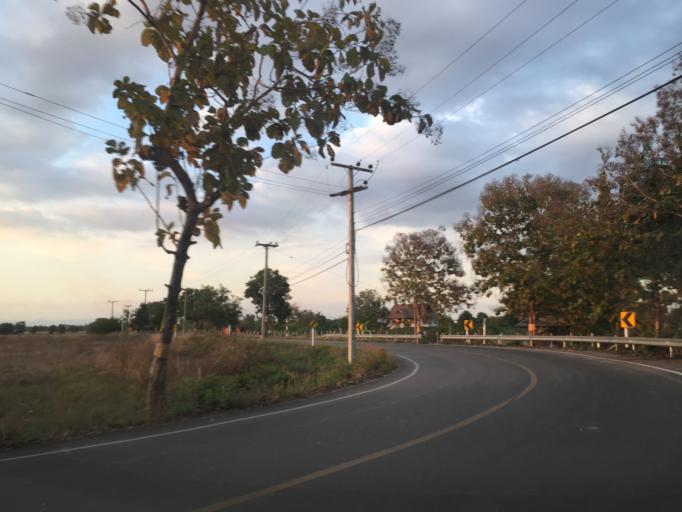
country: TH
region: Lamphun
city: Lamphun
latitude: 18.5145
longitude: 99.0214
